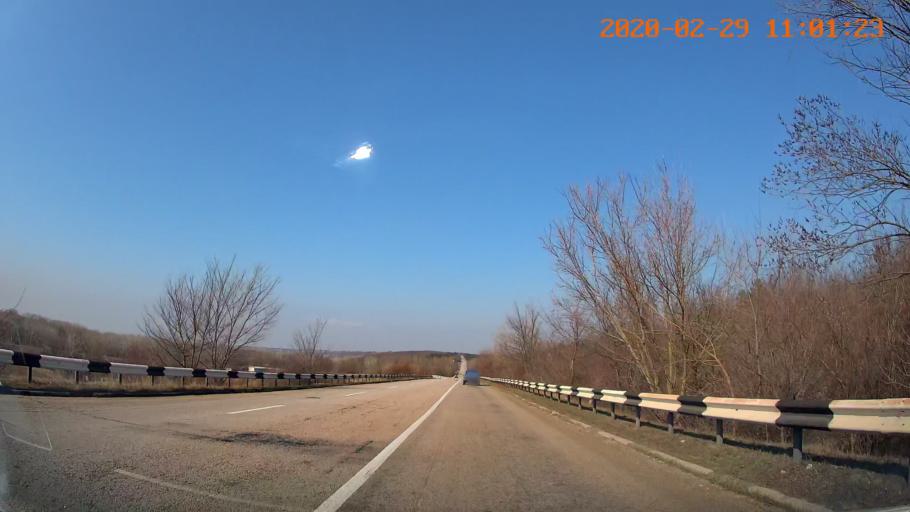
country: MD
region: Telenesti
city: Grigoriopol
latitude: 47.1635
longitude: 29.2597
